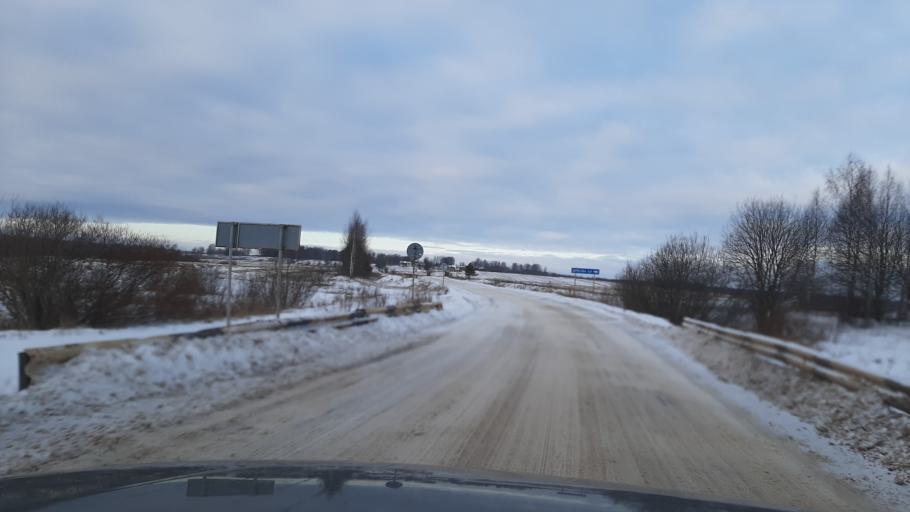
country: RU
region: Kostroma
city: Kosmynino
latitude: 57.4822
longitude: 40.7919
